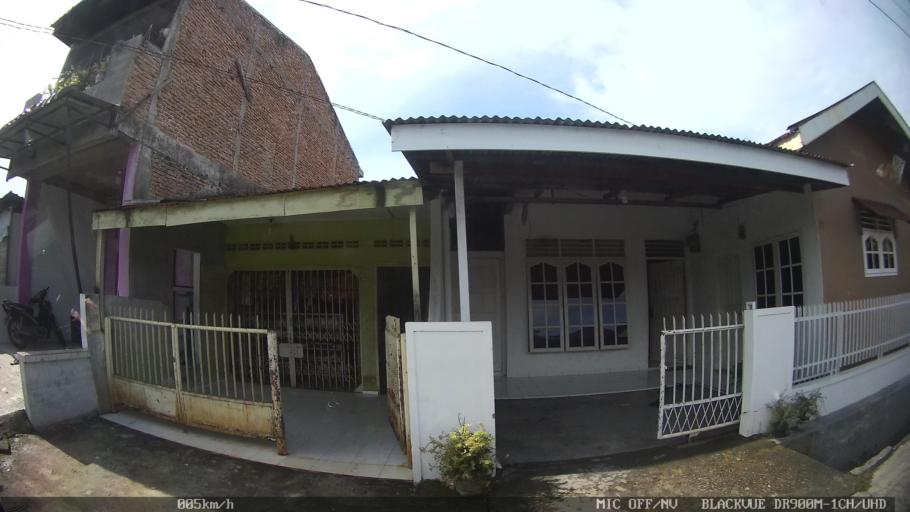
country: ID
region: North Sumatra
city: Medan
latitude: 3.6117
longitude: 98.6507
